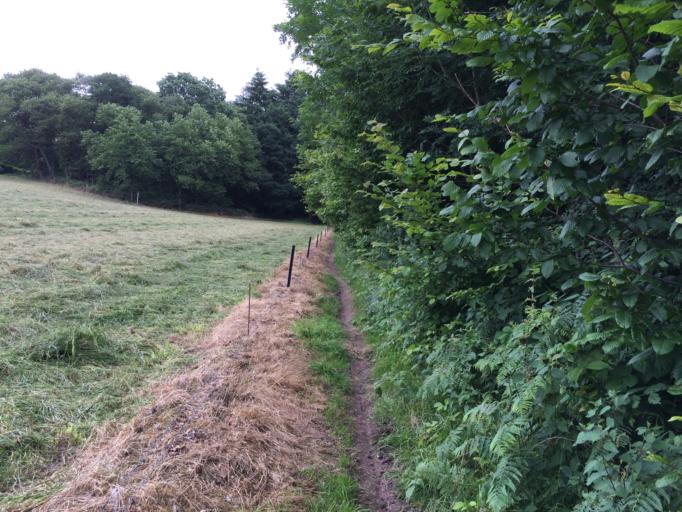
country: BE
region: Wallonia
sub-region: Province de Namur
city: Yvoir
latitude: 50.3417
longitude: 4.9526
